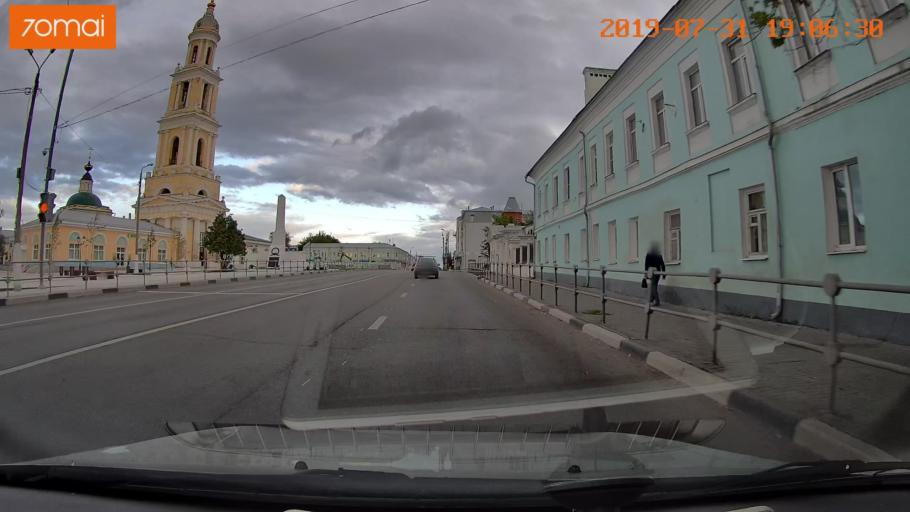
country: RU
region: Moskovskaya
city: Kolomna
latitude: 55.1019
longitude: 38.7539
